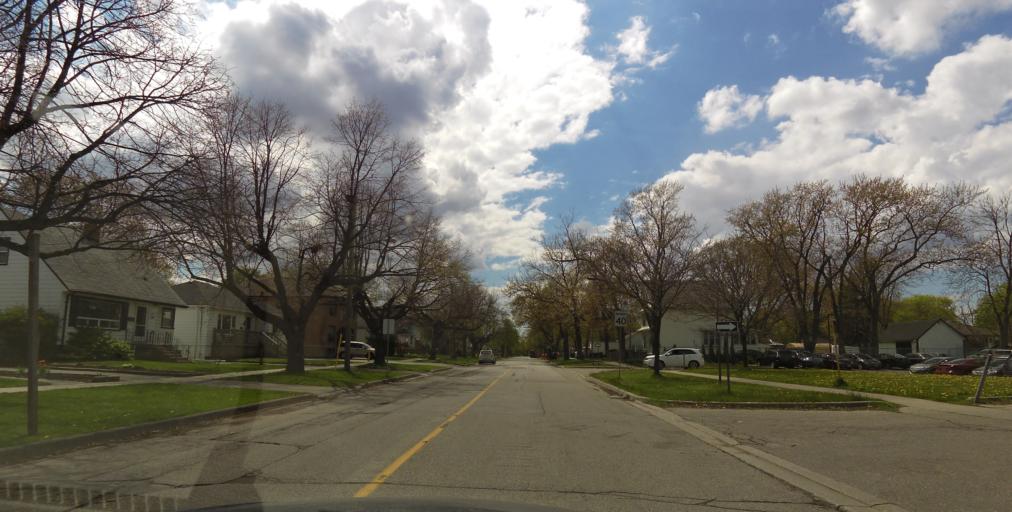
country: CA
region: Ontario
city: Etobicoke
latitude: 43.6010
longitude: -79.5485
